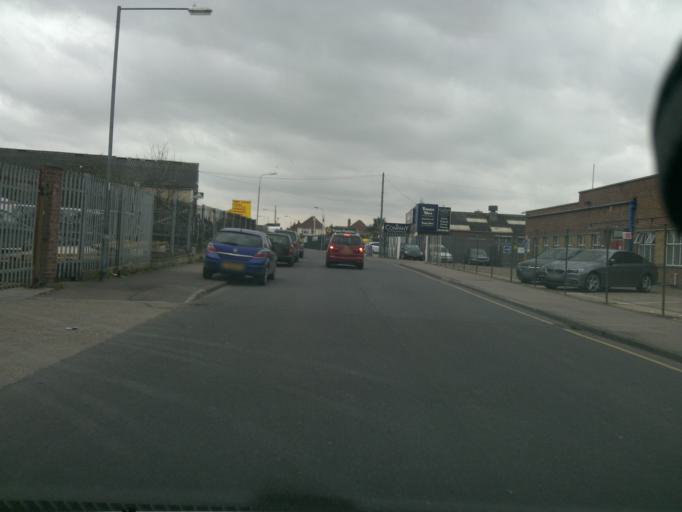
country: GB
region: England
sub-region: Essex
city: Clacton-on-Sea
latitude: 51.8008
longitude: 1.1588
